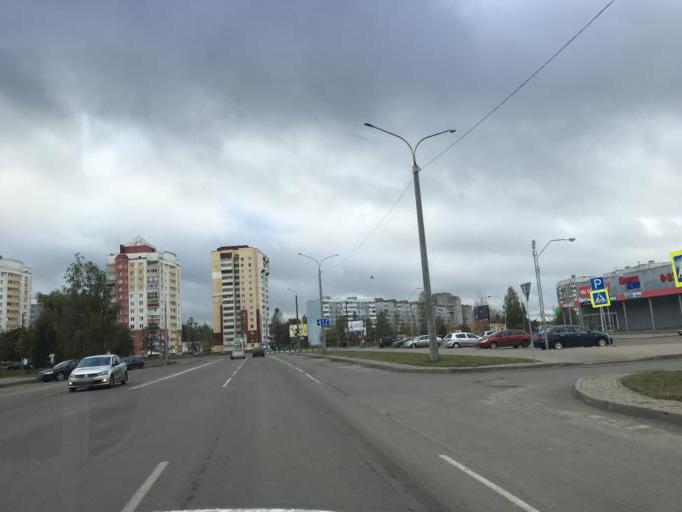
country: BY
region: Mogilev
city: Mahilyow
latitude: 53.8809
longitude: 30.3687
